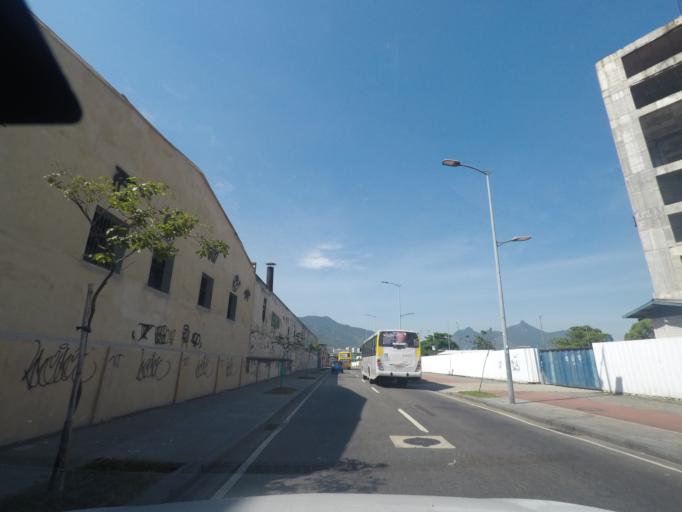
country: BR
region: Rio de Janeiro
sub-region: Rio De Janeiro
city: Rio de Janeiro
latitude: -22.9045
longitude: -43.2073
